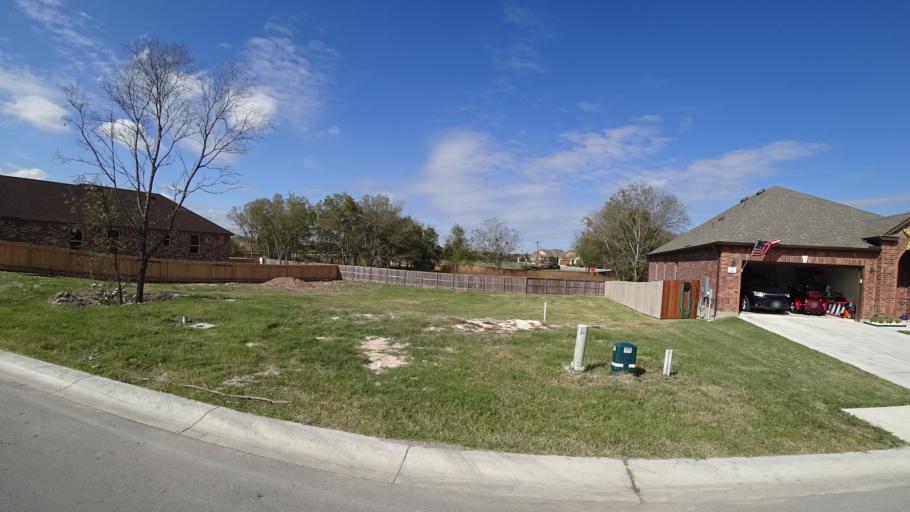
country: US
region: Texas
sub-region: Travis County
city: Pflugerville
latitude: 30.4507
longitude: -97.6288
